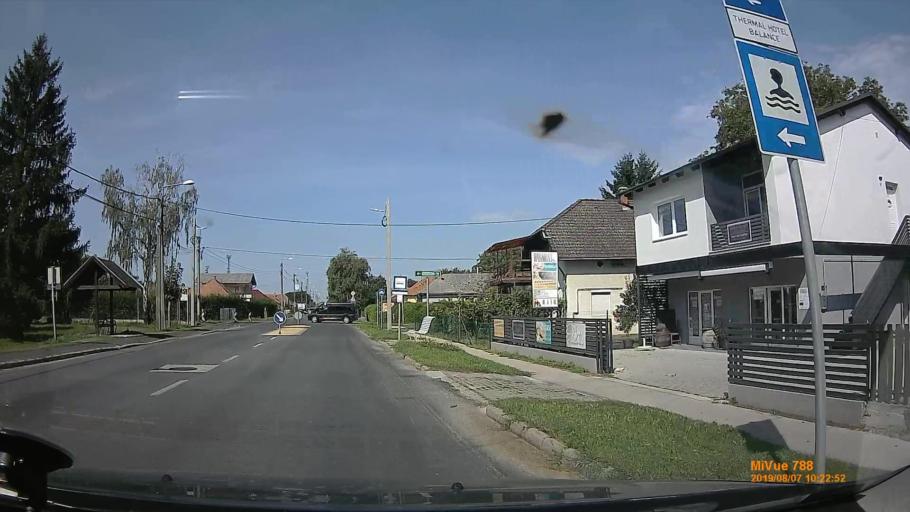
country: HU
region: Zala
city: Lenti
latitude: 46.6225
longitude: 16.5325
